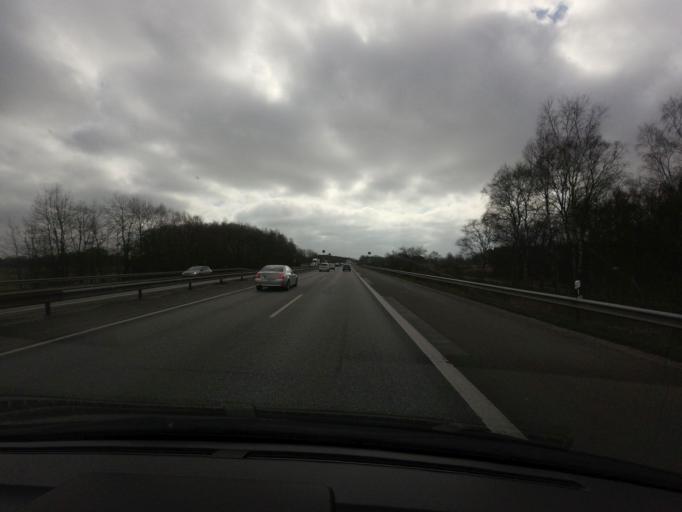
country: DE
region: Schleswig-Holstein
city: Schmalfeld
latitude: 53.8876
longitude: 9.9432
